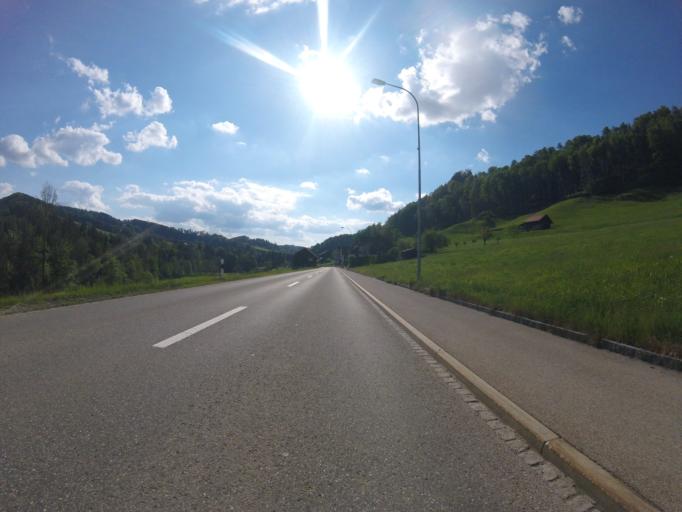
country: CH
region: Saint Gallen
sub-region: Wahlkreis Wil
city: Degersheim
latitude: 47.3632
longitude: 9.1697
